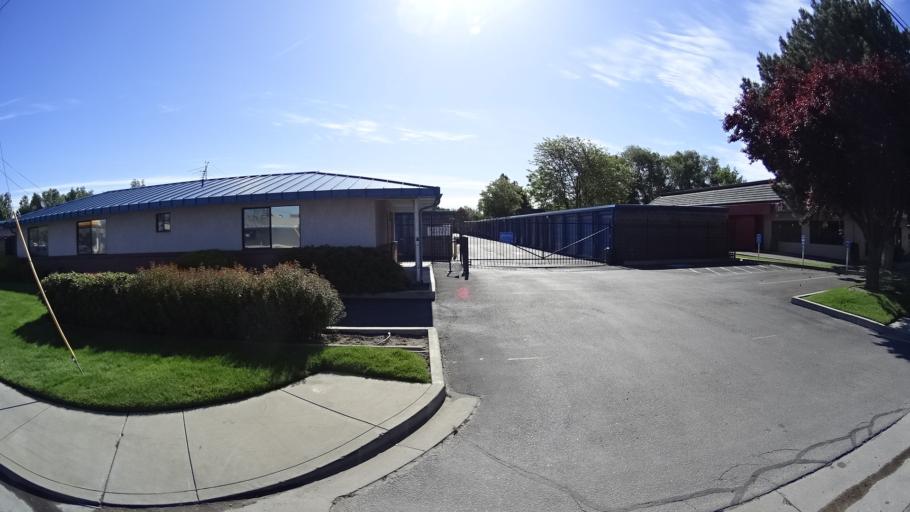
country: US
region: Idaho
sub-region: Ada County
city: Garden City
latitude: 43.5926
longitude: -116.2436
